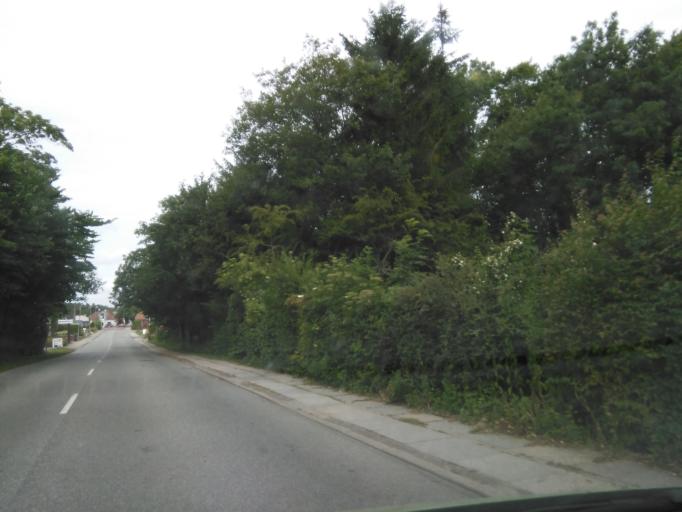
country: DK
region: Central Jutland
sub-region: Arhus Kommune
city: Solbjerg
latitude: 56.0366
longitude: 10.0851
